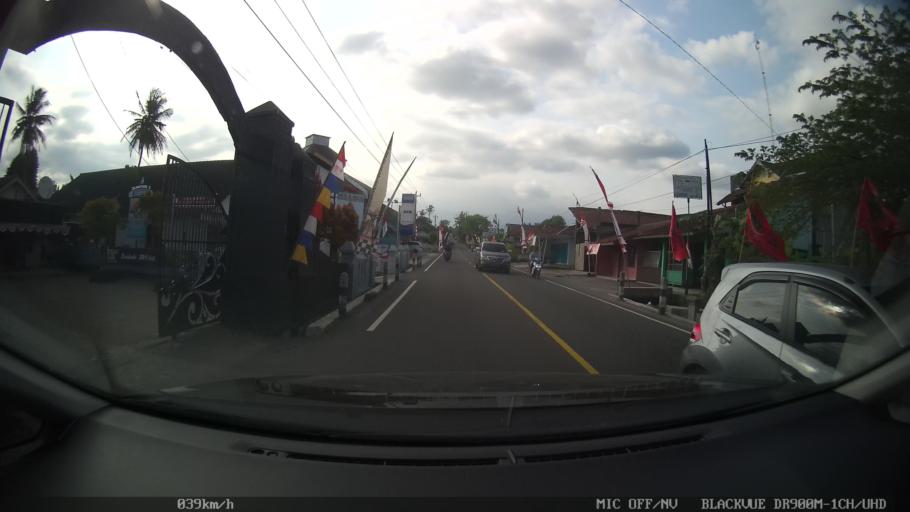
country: ID
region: Central Java
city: Candi Prambanan
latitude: -7.6995
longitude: 110.4656
